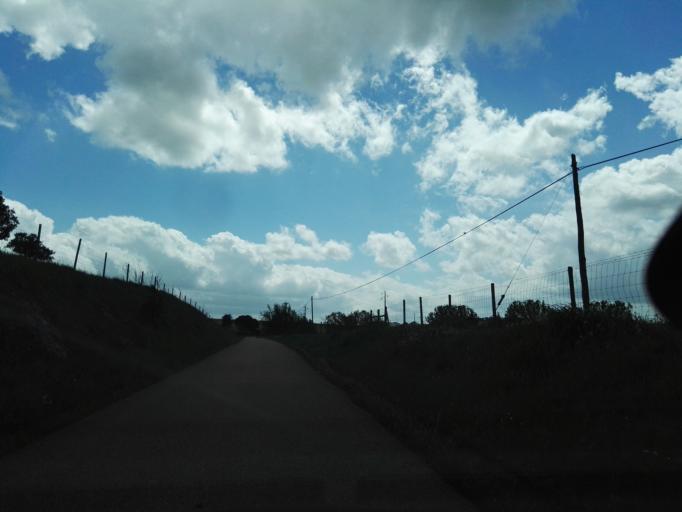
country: PT
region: Portalegre
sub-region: Elvas
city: Elvas
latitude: 38.9697
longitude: -7.1724
